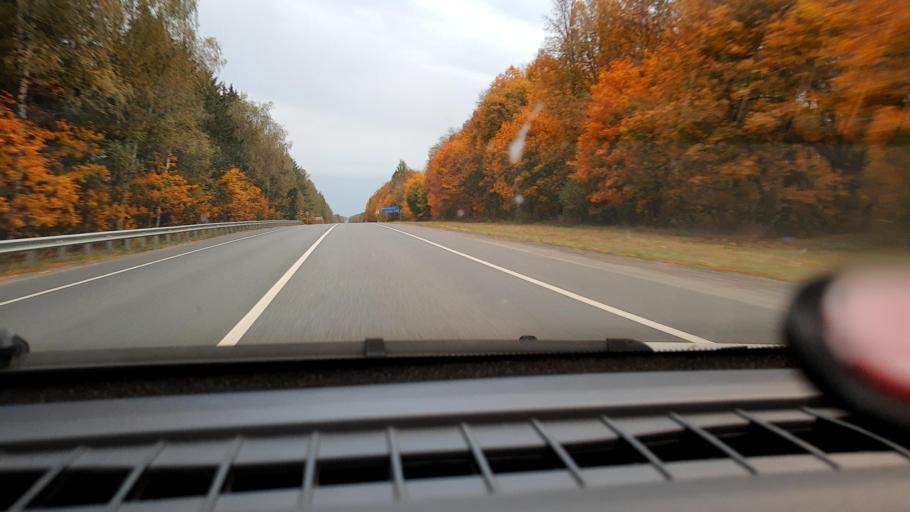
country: RU
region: Vladimir
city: Orgtrud
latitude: 56.1999
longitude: 40.8171
